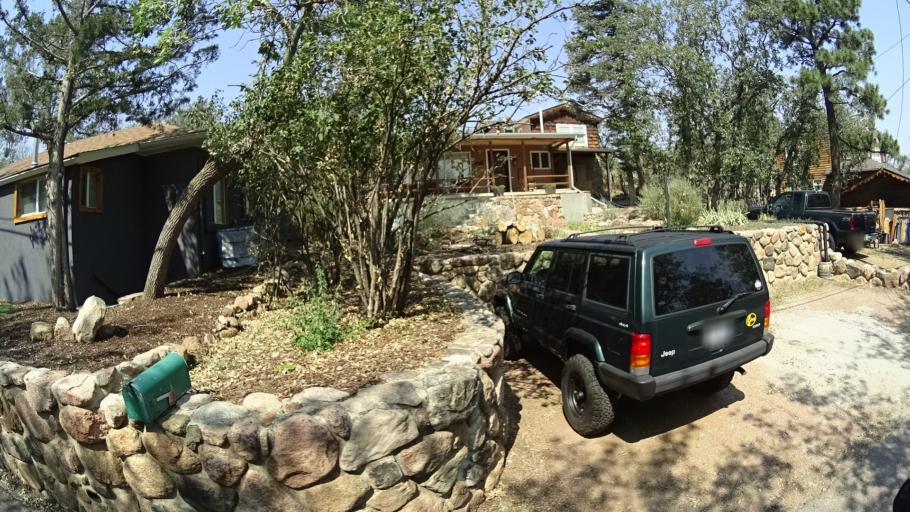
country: US
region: Colorado
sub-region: El Paso County
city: Colorado Springs
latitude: 38.7945
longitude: -104.8578
